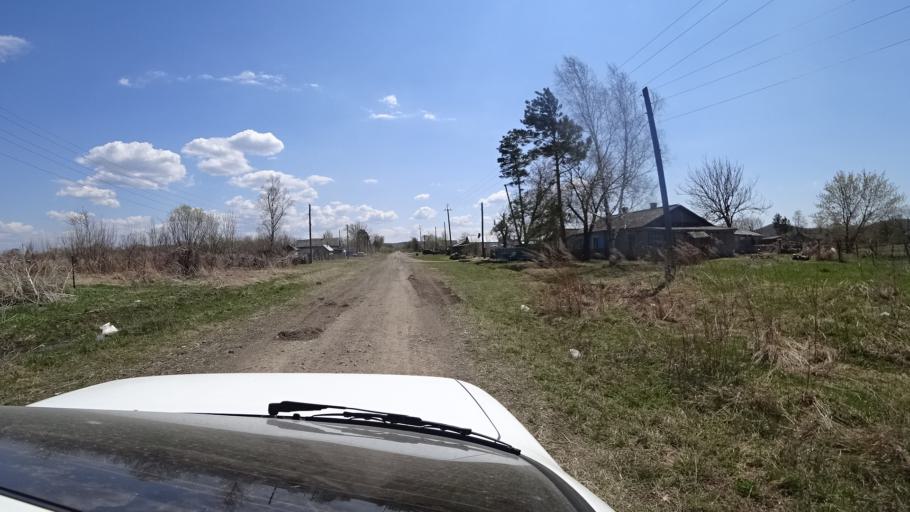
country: RU
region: Primorskiy
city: Lazo
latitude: 45.8021
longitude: 133.7623
